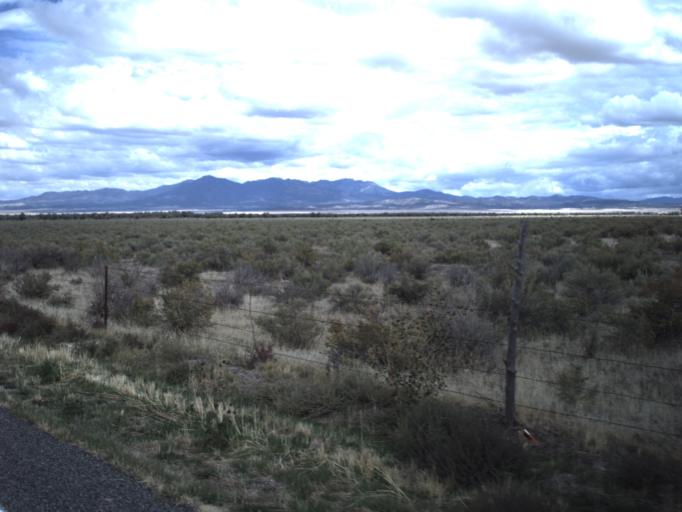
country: US
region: Utah
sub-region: Millard County
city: Fillmore
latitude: 39.0788
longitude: -112.4098
